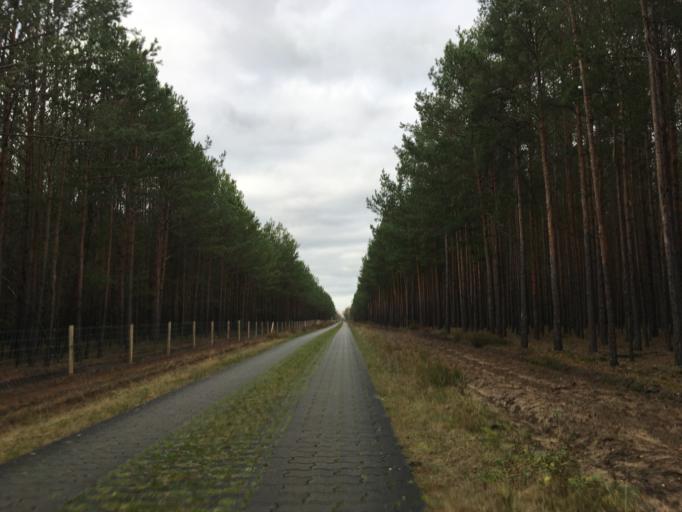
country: DE
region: Brandenburg
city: Tauer
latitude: 51.9956
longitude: 14.5133
